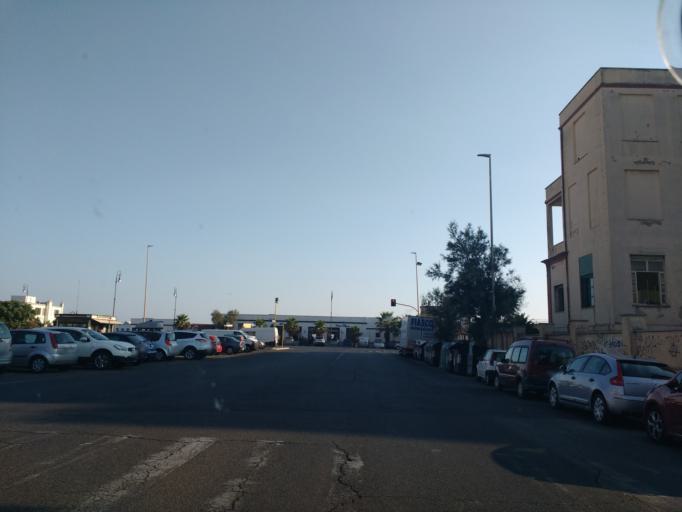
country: IT
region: Latium
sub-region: Citta metropolitana di Roma Capitale
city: Lido di Ostia
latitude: 41.7317
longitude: 12.2729
